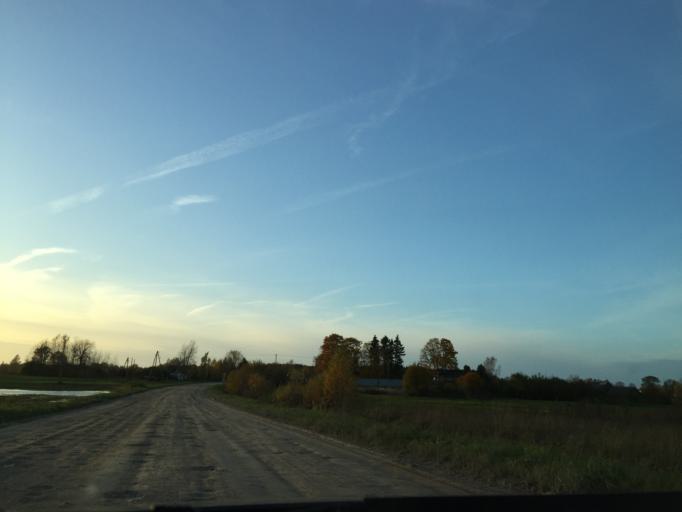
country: LV
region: Malpils
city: Malpils
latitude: 56.8924
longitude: 24.9375
